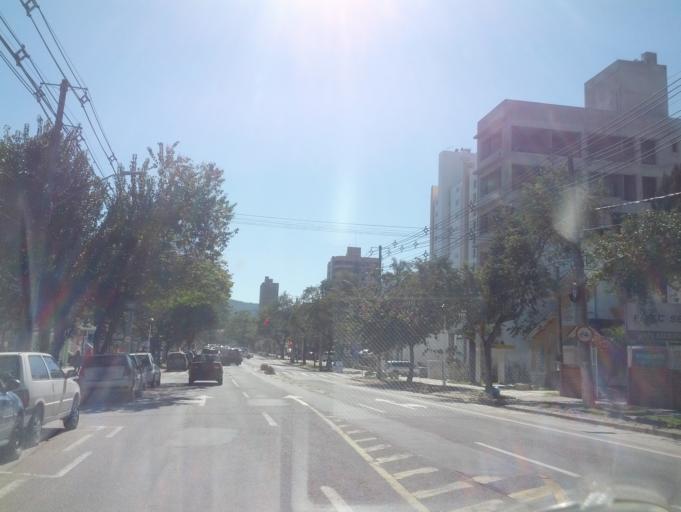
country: BR
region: Santa Catarina
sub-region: Blumenau
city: Blumenau
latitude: -26.9272
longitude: -49.0618
